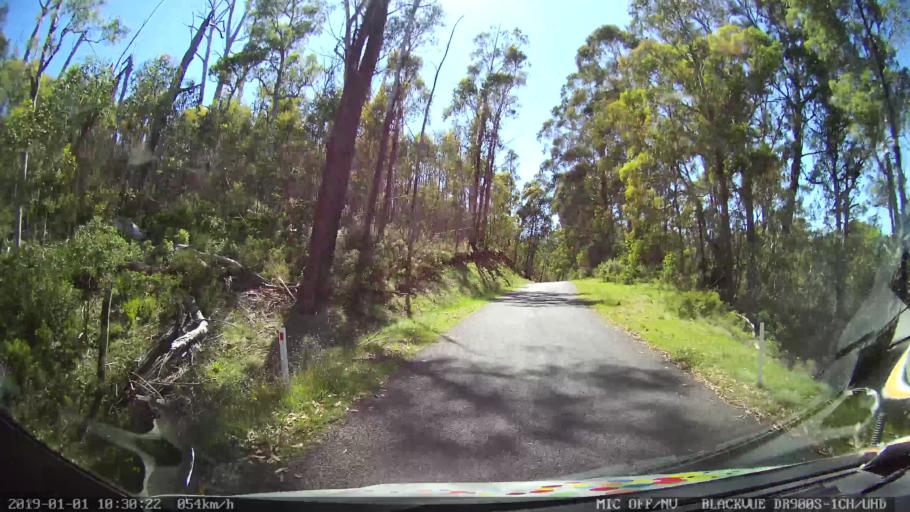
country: AU
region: New South Wales
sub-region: Snowy River
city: Jindabyne
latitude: -36.0522
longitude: 148.2576
